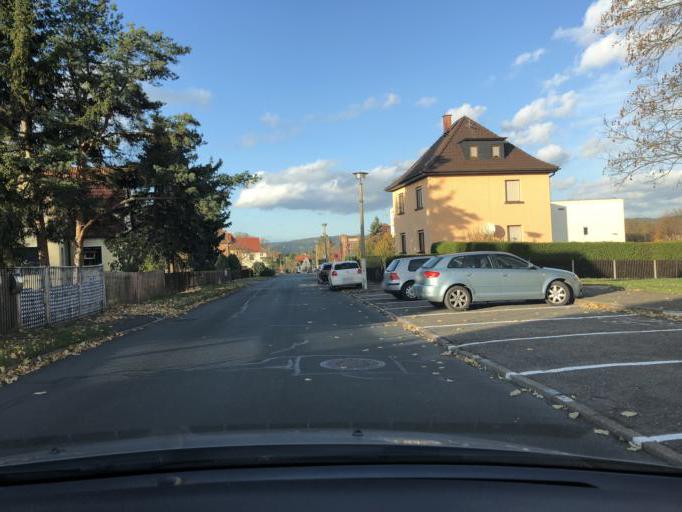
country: DE
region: Thuringia
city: Bodelwitz
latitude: 50.6978
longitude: 11.6107
